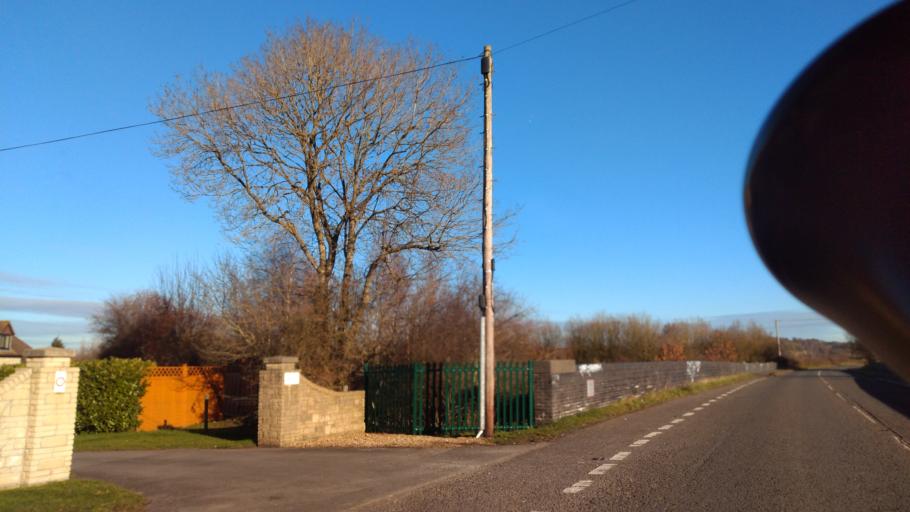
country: GB
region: England
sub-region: Somerset
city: Frome
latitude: 51.2304
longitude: -2.2995
